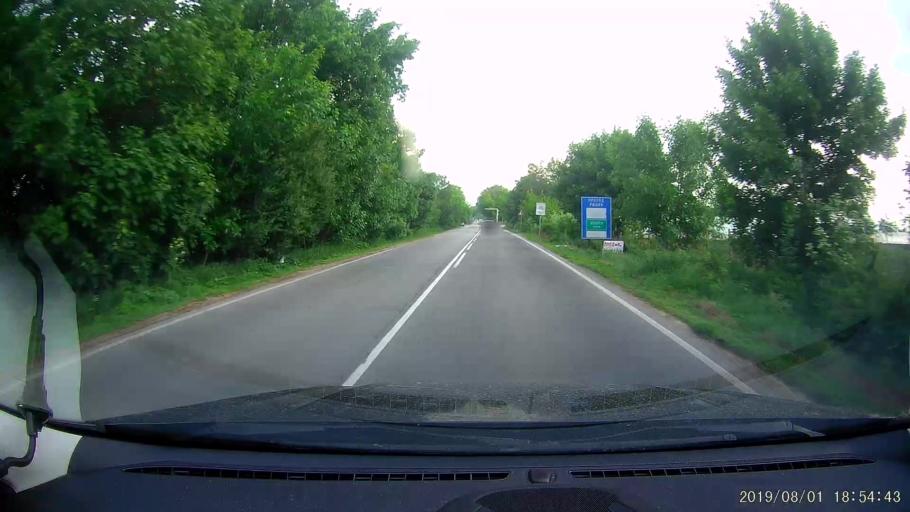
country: BG
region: Shumen
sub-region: Obshtina Shumen
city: Shumen
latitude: 43.1920
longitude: 27.0031
